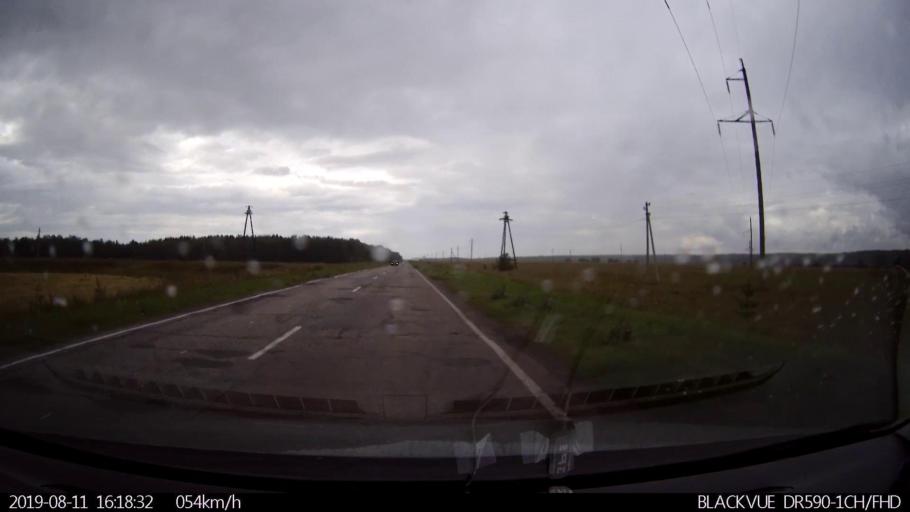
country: RU
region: Ulyanovsk
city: Mayna
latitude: 54.0566
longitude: 47.6112
